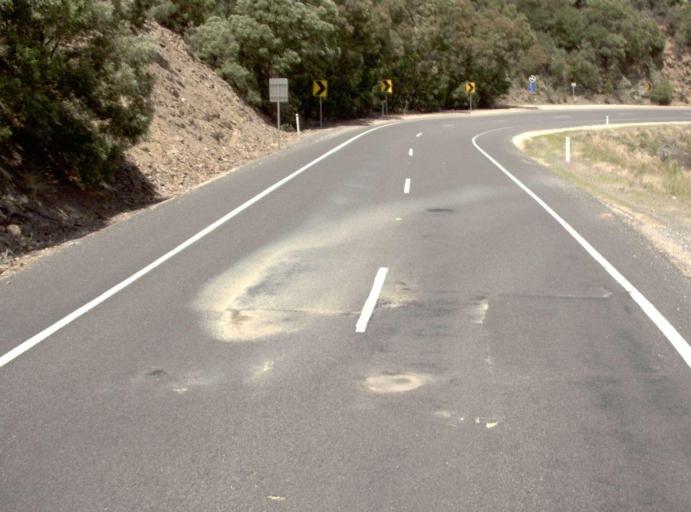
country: AU
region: Victoria
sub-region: East Gippsland
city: Lakes Entrance
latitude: -37.5519
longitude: 147.8713
